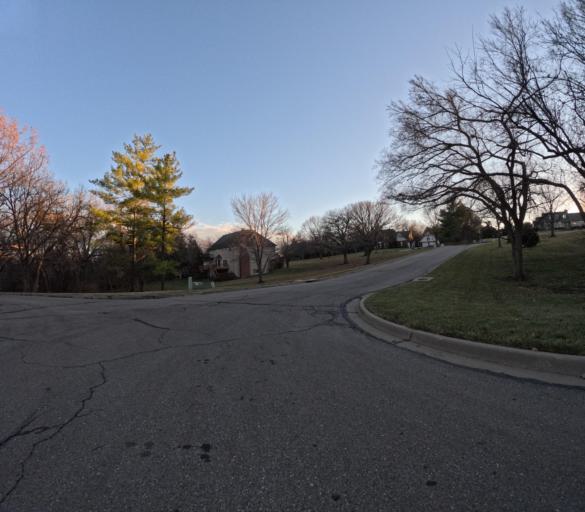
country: US
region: Kansas
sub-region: Riley County
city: Manhattan
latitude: 39.1915
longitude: -96.6304
